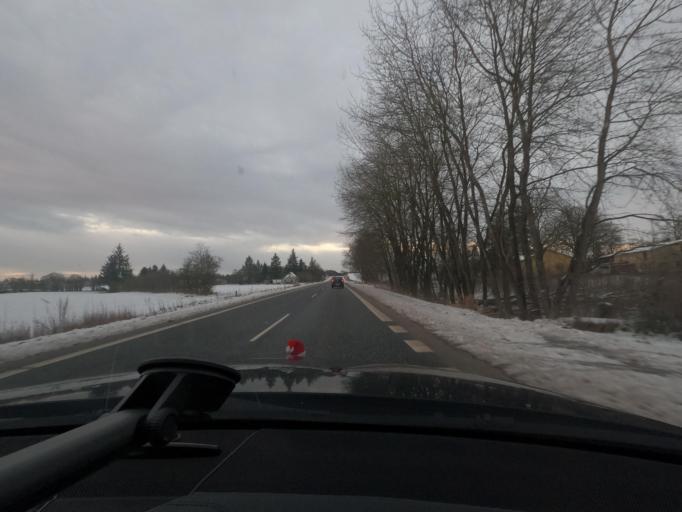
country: DK
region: South Denmark
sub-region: Aabenraa Kommune
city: Krusa
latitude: 54.8662
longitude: 9.4542
